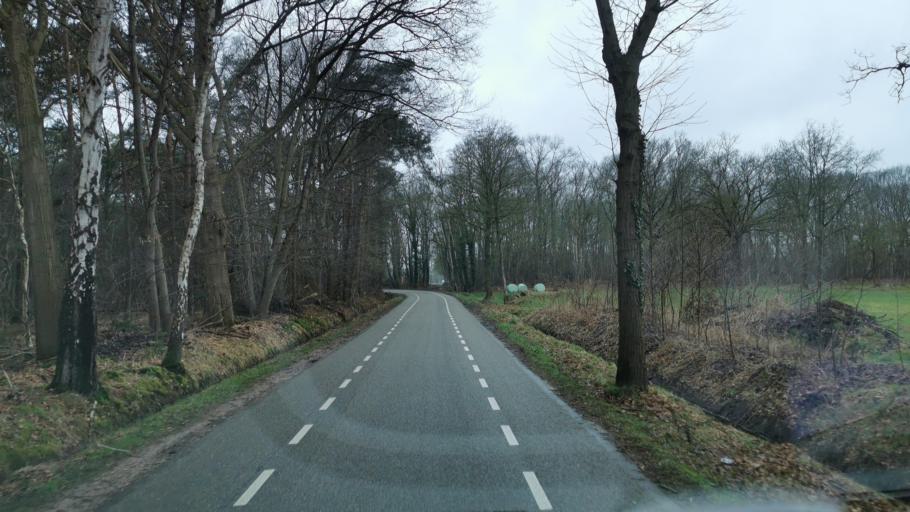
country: NL
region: Overijssel
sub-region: Gemeente Borne
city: Borne
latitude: 52.3279
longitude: 6.7922
